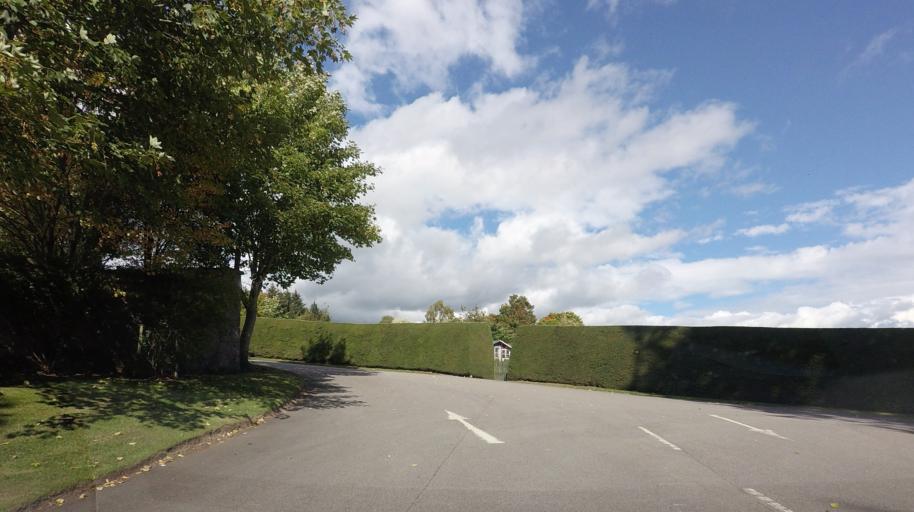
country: GB
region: Scotland
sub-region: Aberdeenshire
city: Banchory
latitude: 57.0615
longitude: -2.4380
